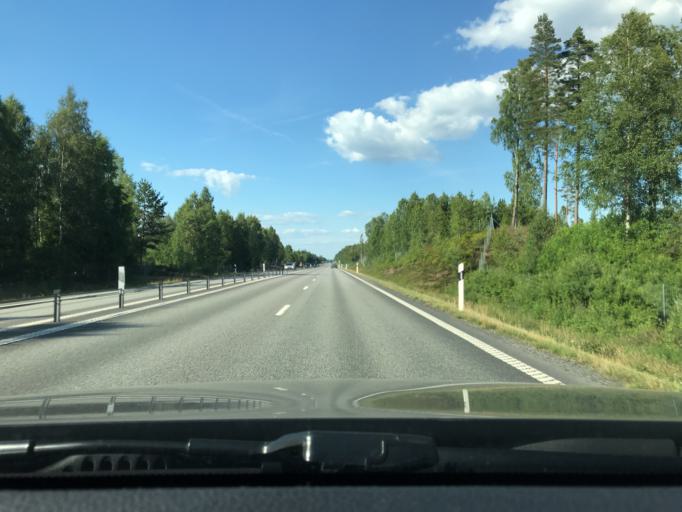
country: SE
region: Kronoberg
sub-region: Almhults Kommun
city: AElmhult
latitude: 56.4782
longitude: 14.1095
